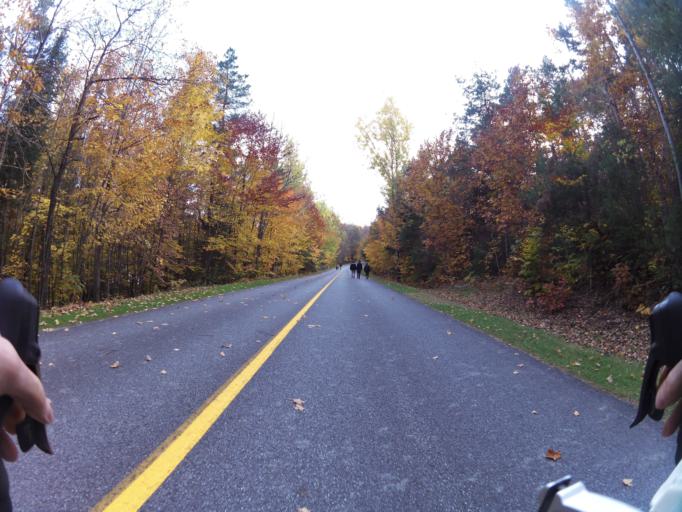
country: CA
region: Quebec
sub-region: Outaouais
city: Wakefield
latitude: 45.6122
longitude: -76.0112
